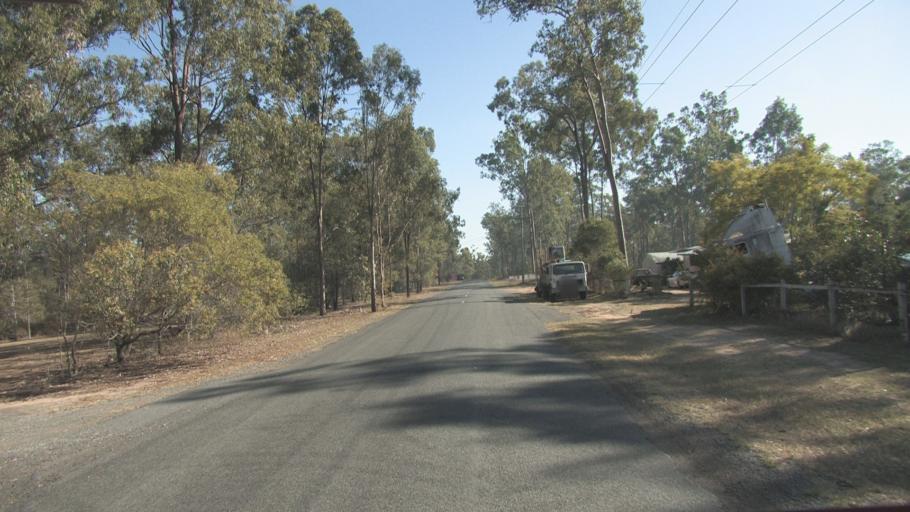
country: AU
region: Queensland
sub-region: Logan
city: Cedar Vale
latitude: -27.8445
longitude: 153.0578
